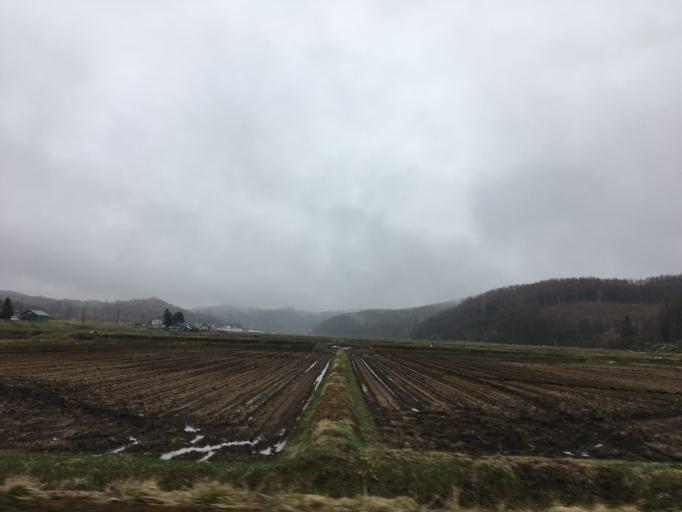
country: JP
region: Hokkaido
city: Nayoro
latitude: 44.0805
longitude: 142.4182
